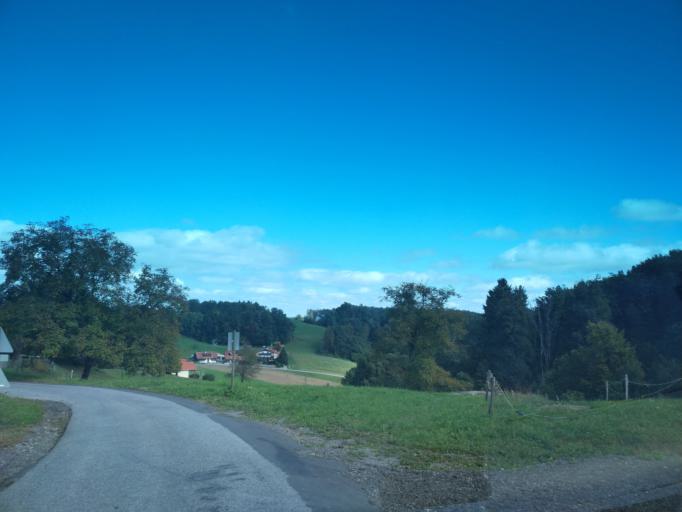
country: AT
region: Styria
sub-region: Politischer Bezirk Leibnitz
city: Grossklein
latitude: 46.7287
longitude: 15.4661
